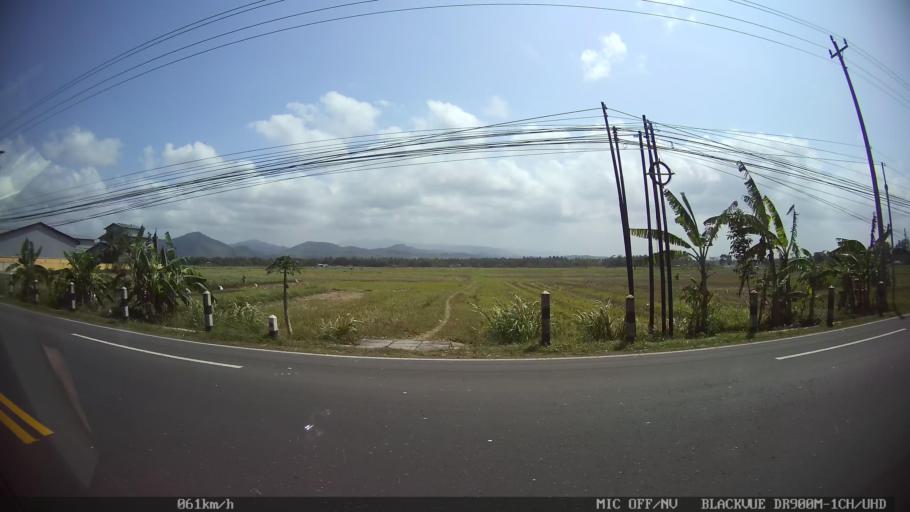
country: ID
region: Daerah Istimewa Yogyakarta
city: Srandakan
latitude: -7.8911
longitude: 110.1213
